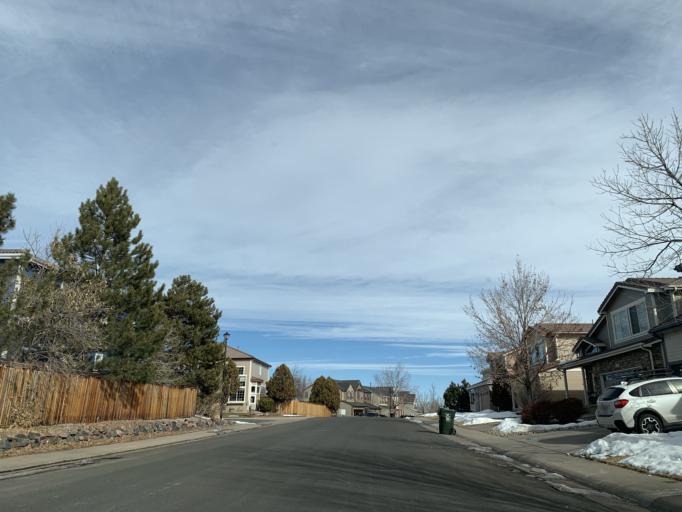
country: US
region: Colorado
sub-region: Douglas County
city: Carriage Club
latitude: 39.5321
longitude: -104.9371
